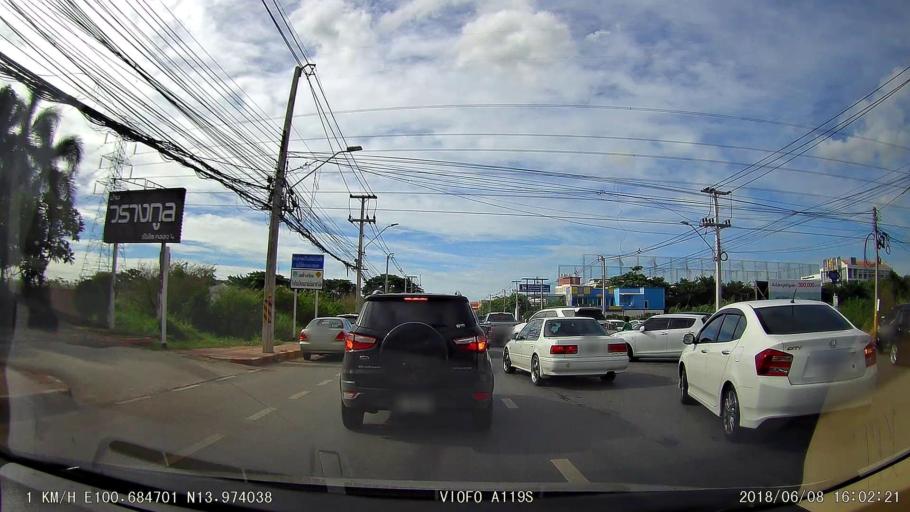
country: TH
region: Pathum Thani
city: Thanyaburi
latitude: 13.9765
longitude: 100.6848
